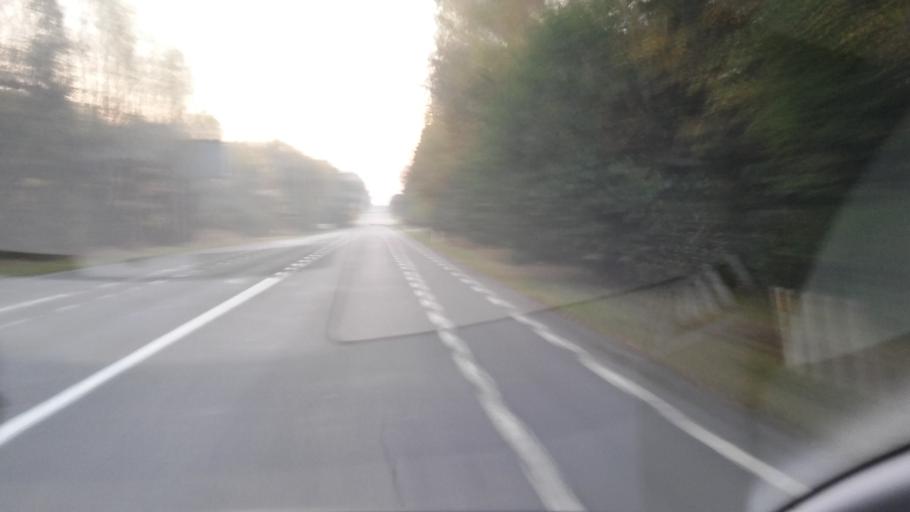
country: BE
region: Wallonia
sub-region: Province du Luxembourg
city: Arlon
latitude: 49.6863
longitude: 5.7470
